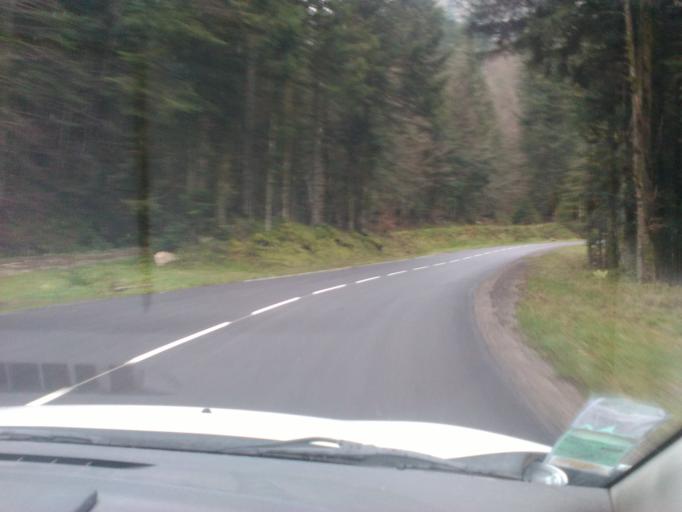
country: FR
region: Lorraine
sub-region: Departement des Vosges
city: Xonrupt-Longemer
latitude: 48.0527
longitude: 6.9890
